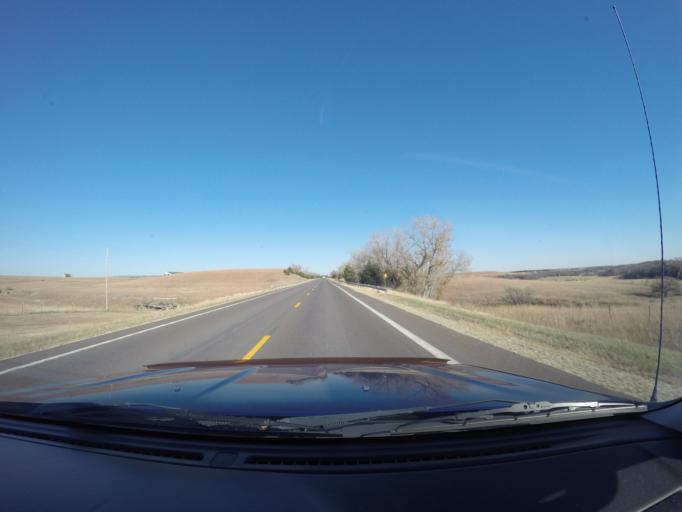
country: US
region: Kansas
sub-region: Marshall County
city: Blue Rapids
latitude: 39.4449
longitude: -96.7643
